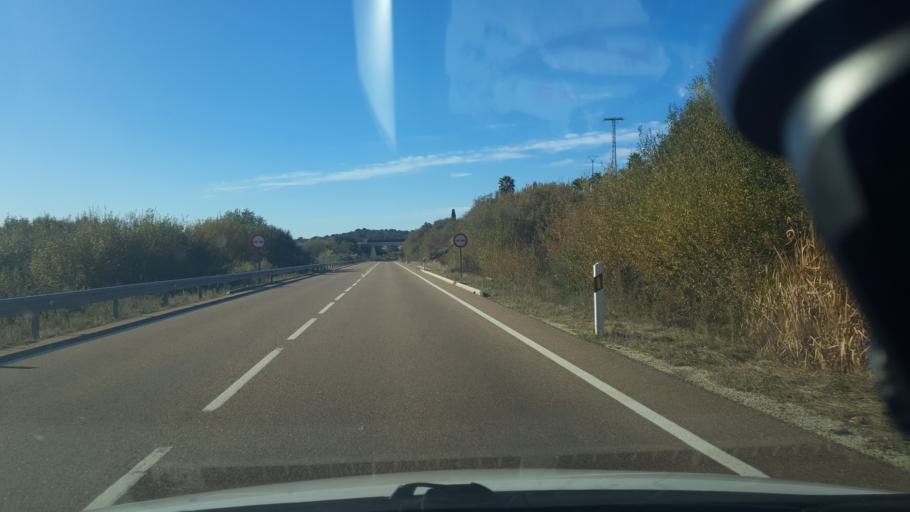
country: ES
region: Castille and Leon
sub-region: Provincia de Avila
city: Poyales del Hoyo
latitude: 40.1619
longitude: -5.1453
